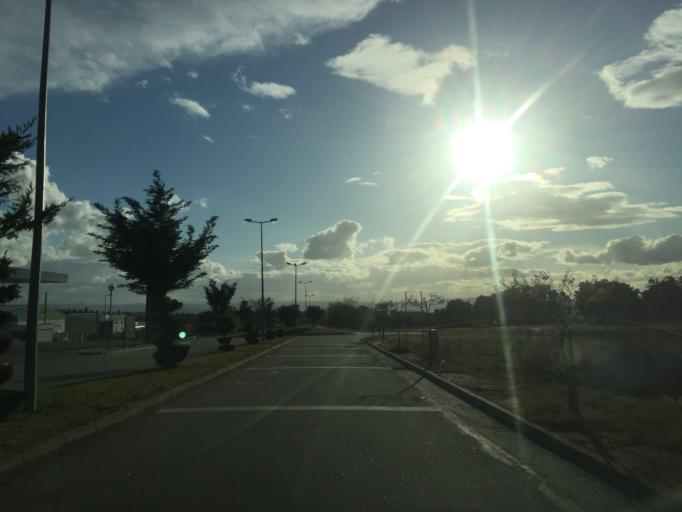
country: PT
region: Braganca
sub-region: Alfandega da Fe
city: Alfandega da Fe
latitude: 41.3326
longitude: -6.9685
